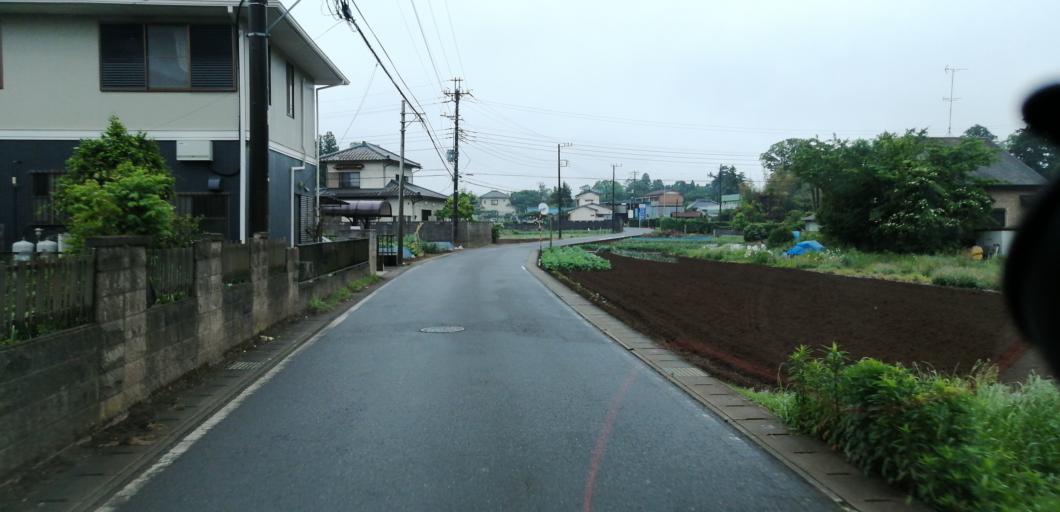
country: JP
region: Chiba
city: Oami
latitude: 35.5814
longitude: 140.2675
